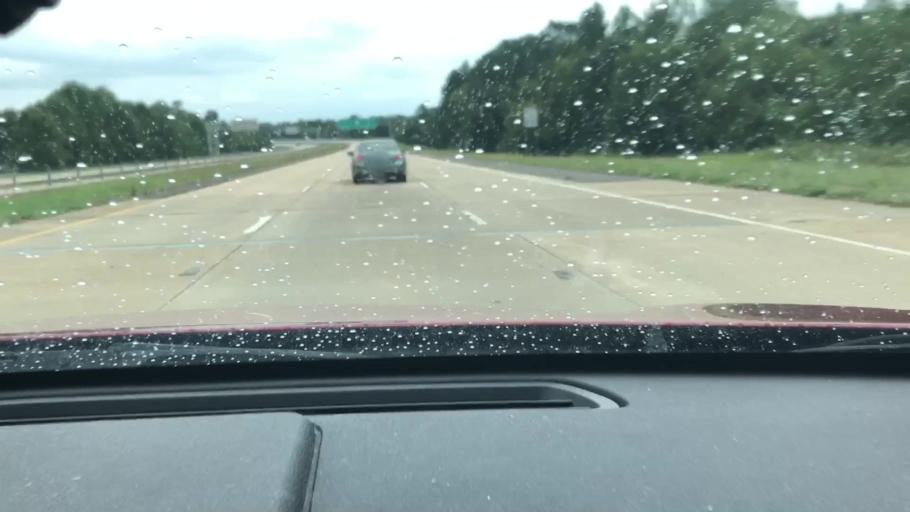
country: US
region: Texas
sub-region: Bowie County
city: Texarkana
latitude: 33.3854
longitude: -94.0367
